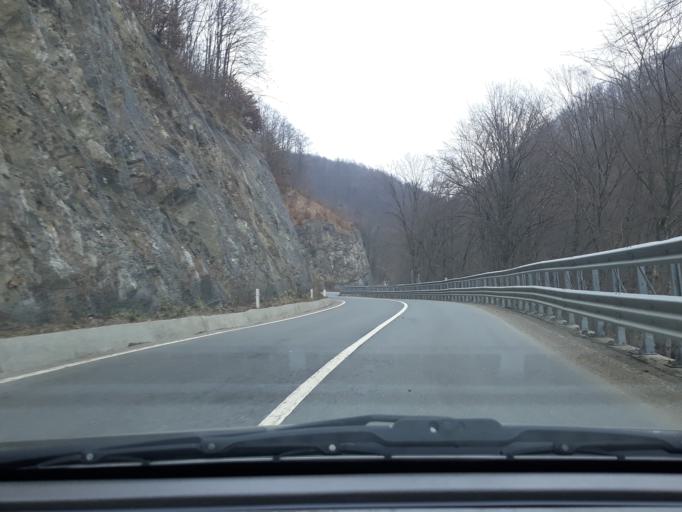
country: RO
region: Bihor
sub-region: Oras Alesd
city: Pestis
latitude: 47.1166
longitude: 22.4096
